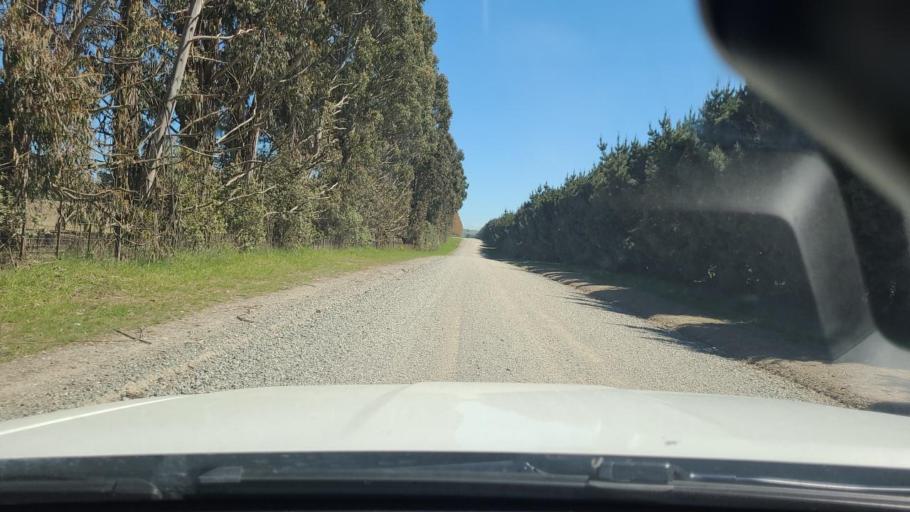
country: NZ
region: Southland
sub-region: Gore District
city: Gore
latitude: -45.7913
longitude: 168.6769
